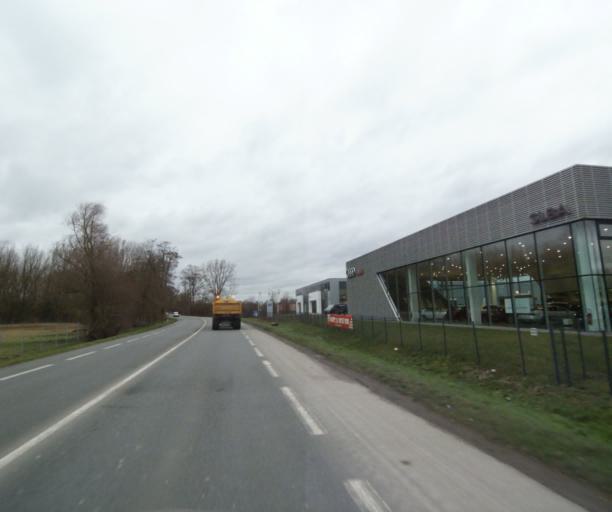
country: FR
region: Nord-Pas-de-Calais
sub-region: Departement du Nord
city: Bruay-sur-l'Escaut
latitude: 50.3888
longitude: 3.5488
